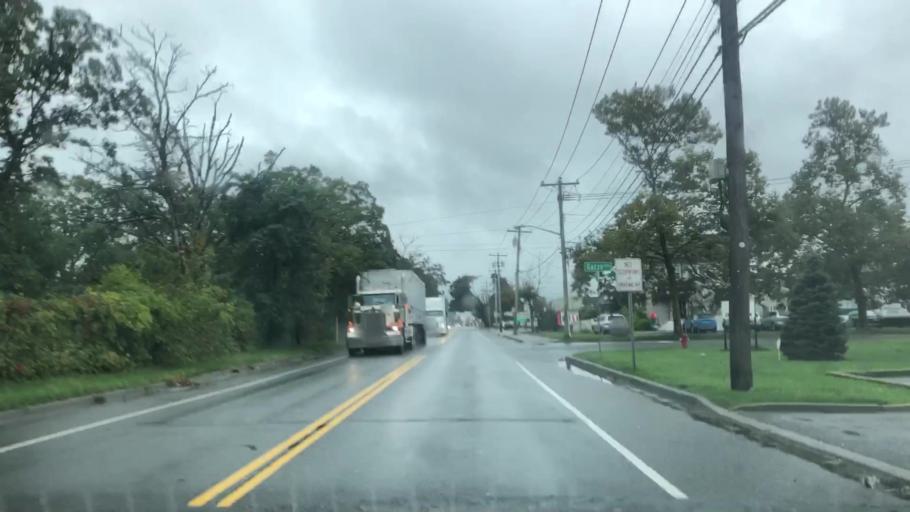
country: US
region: New York
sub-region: Suffolk County
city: East Farmingdale
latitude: 40.7472
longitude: -73.4142
